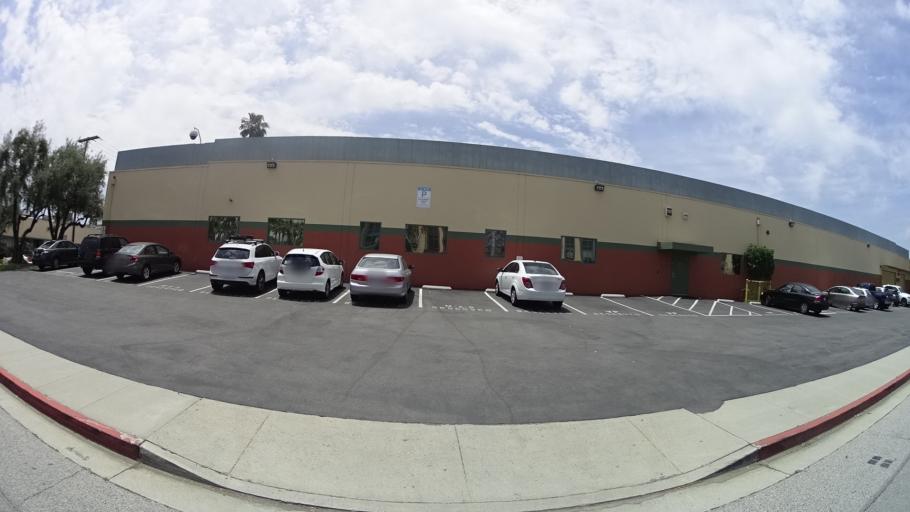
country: US
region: California
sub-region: Los Angeles County
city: North Glendale
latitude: 34.1598
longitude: -118.2871
